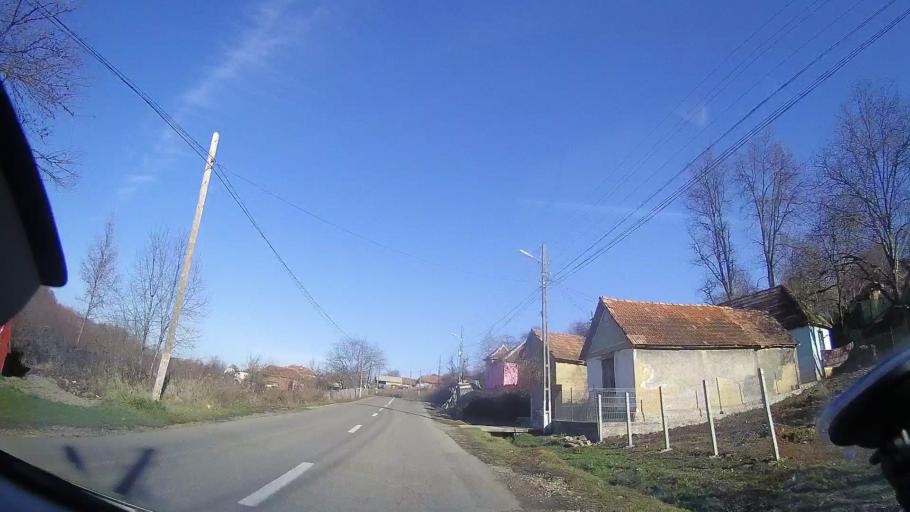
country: RO
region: Bihor
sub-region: Comuna Bratca
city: Bratca
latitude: 46.9325
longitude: 22.6024
